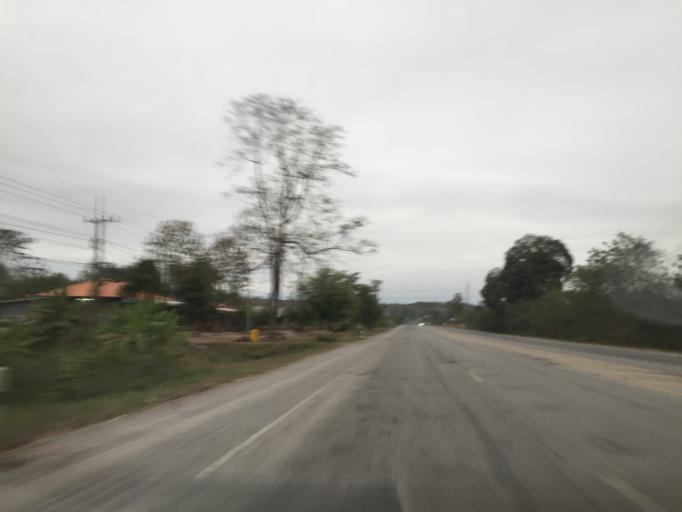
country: TH
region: Loei
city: Erawan
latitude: 17.3143
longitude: 101.9176
